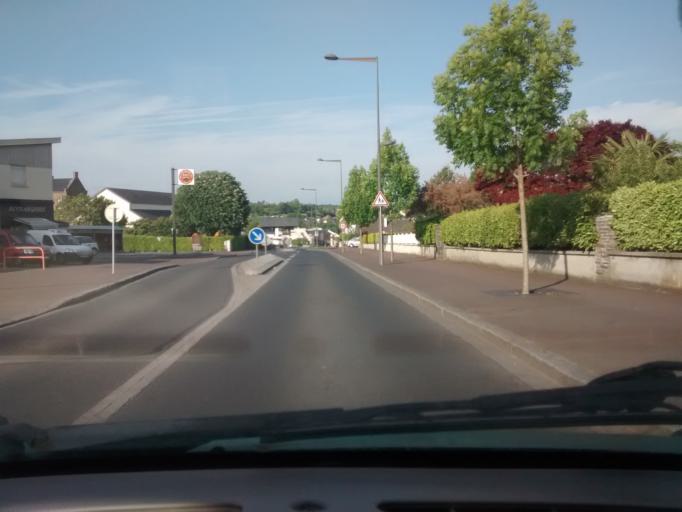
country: FR
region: Lower Normandy
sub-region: Departement de la Manche
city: Agneaux
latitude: 49.1176
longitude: -1.1086
